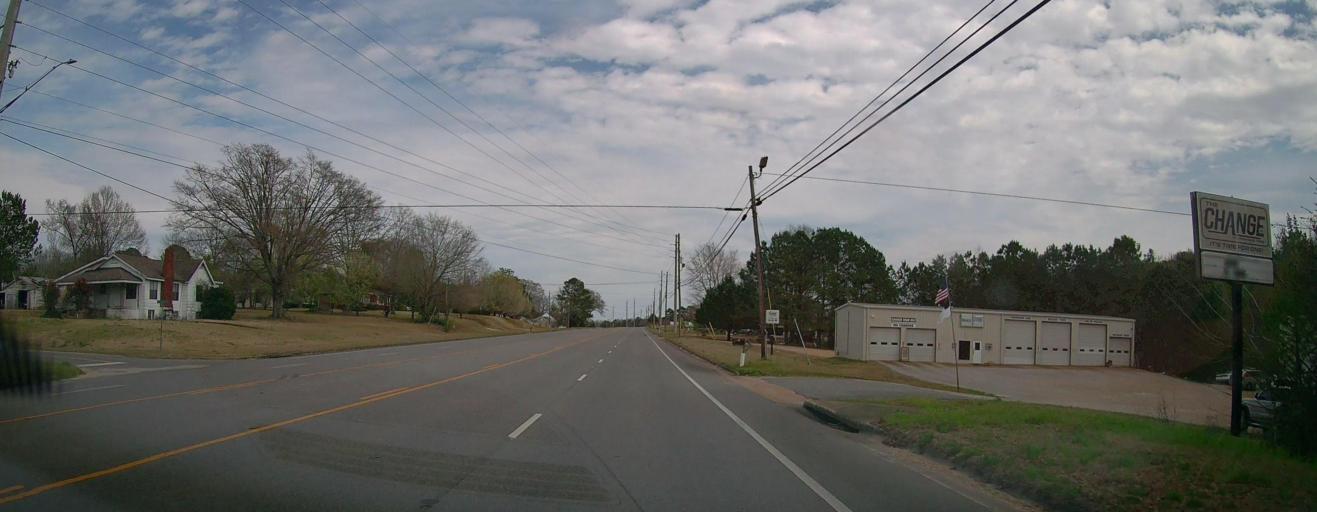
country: US
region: Alabama
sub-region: Marion County
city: Winfield
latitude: 33.9308
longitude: -87.7788
